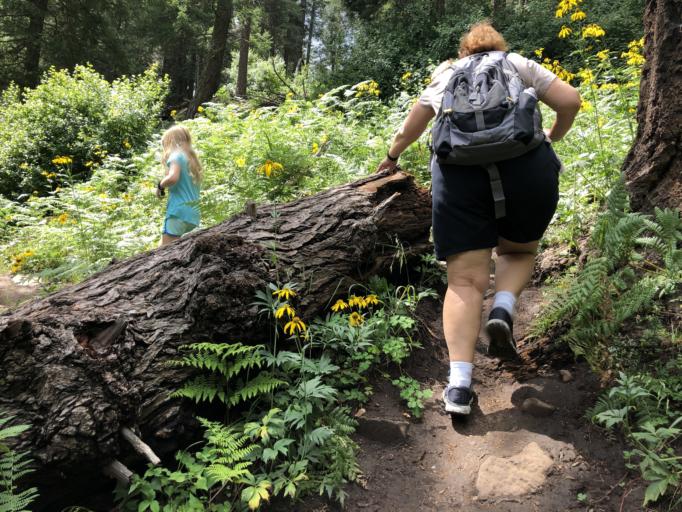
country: US
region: Arizona
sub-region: Gila County
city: Star Valley
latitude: 34.3395
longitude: -110.9552
